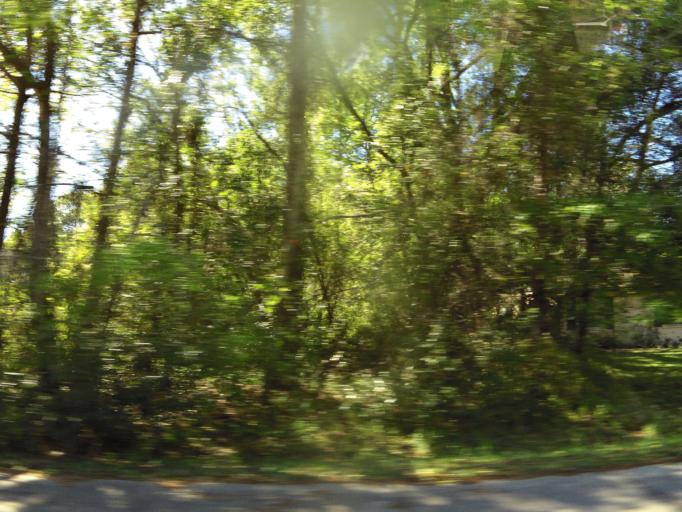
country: US
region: Florida
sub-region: Bradford County
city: Starke
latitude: 29.9333
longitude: -82.1023
